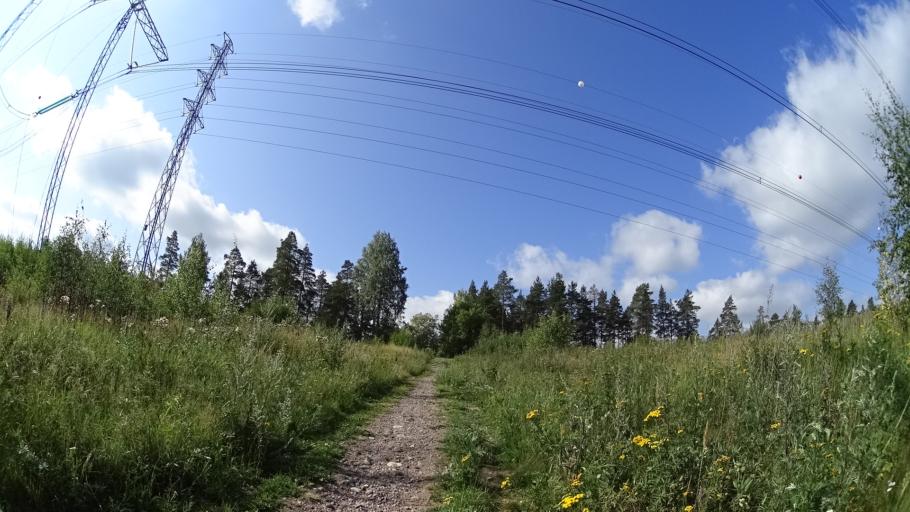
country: FI
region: Uusimaa
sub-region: Helsinki
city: Teekkarikylae
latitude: 60.2929
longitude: 24.9043
